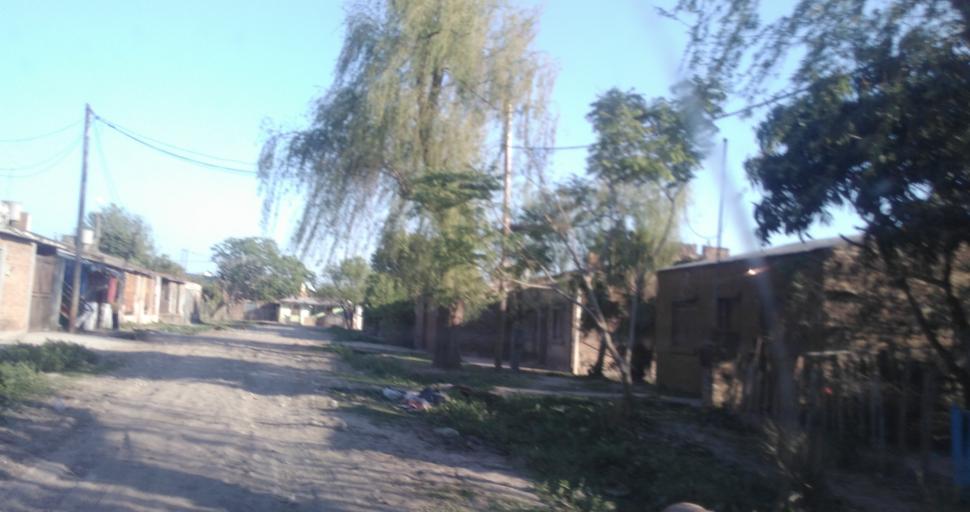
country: AR
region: Chaco
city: Resistencia
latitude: -27.4641
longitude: -59.0176
